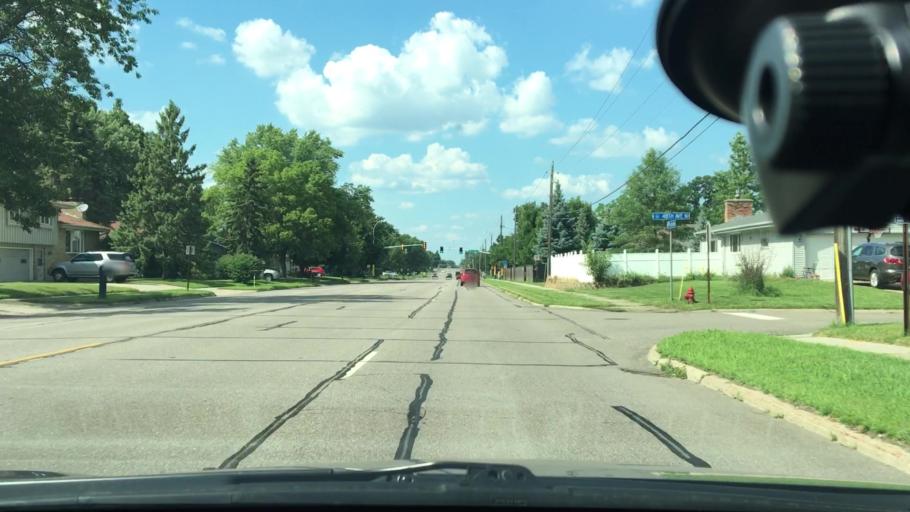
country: US
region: Minnesota
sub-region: Hennepin County
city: New Hope
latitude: 45.0422
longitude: -93.3803
